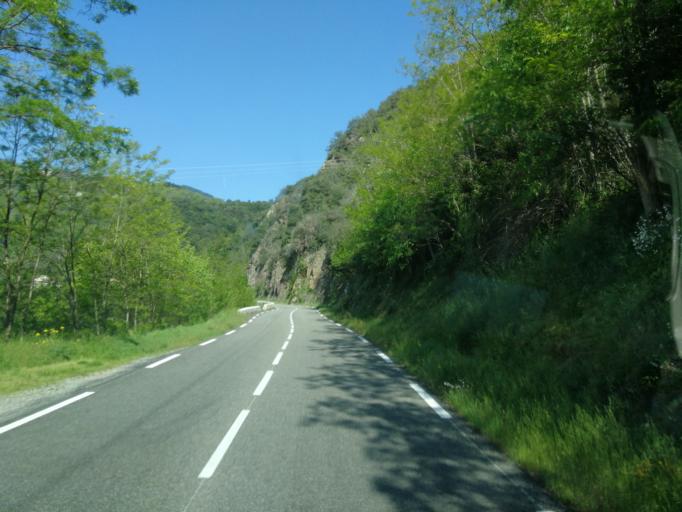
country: FR
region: Rhone-Alpes
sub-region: Departement de l'Ardeche
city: Saint-Sauveur-de-Montagut
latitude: 44.8528
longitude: 4.5701
